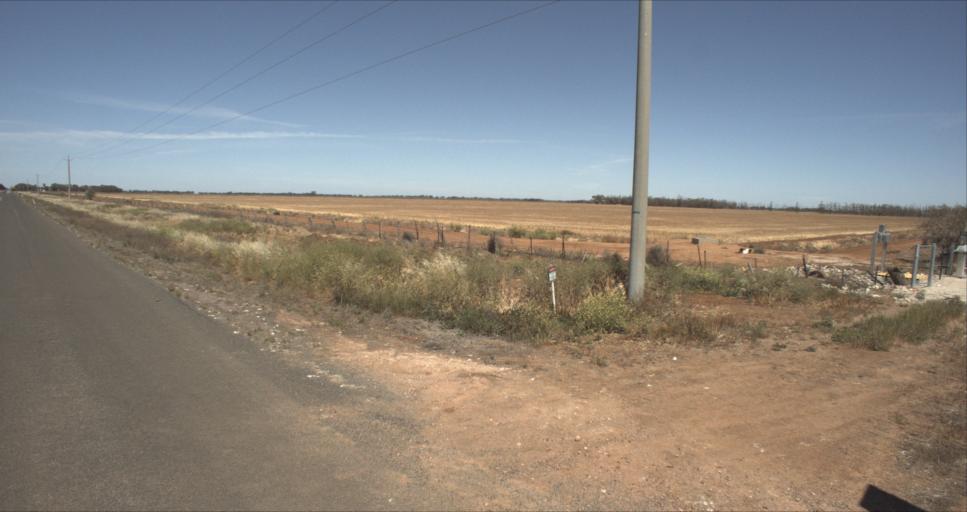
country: AU
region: New South Wales
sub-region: Leeton
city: Leeton
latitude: -34.4822
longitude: 146.2903
